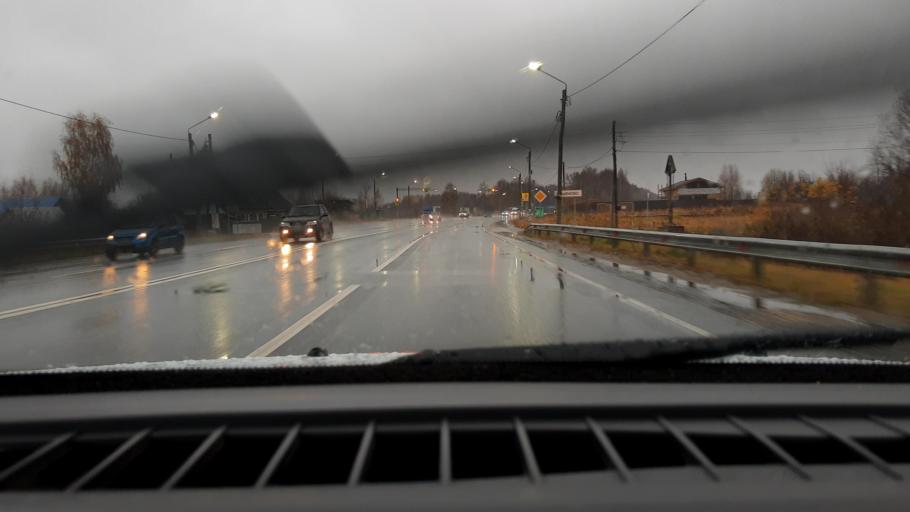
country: RU
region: Nizjnij Novgorod
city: Sitniki
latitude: 56.5054
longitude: 44.0239
